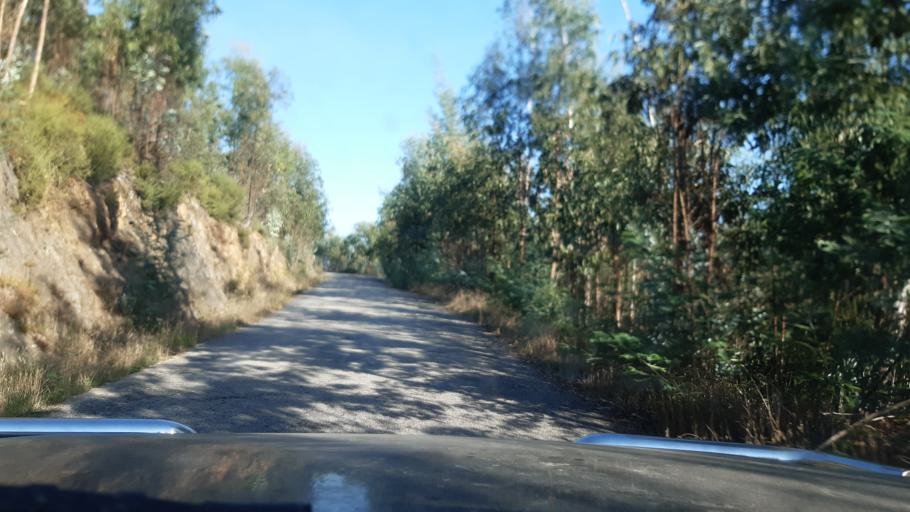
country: PT
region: Aveiro
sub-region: Agueda
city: Aguada de Cima
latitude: 40.5645
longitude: -8.3356
